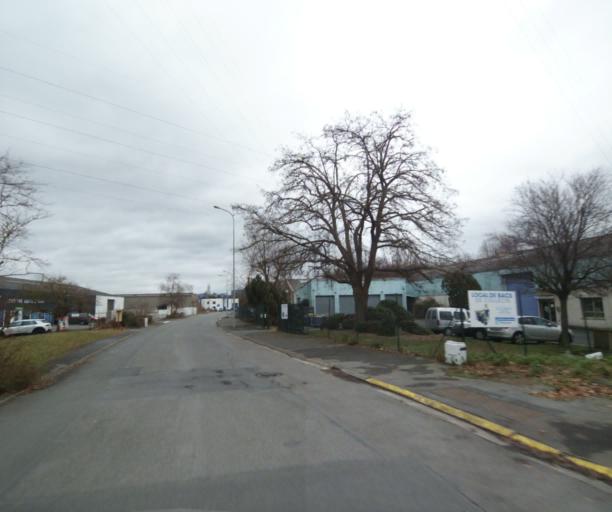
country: FR
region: Nord-Pas-de-Calais
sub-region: Departement du Nord
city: Saint-Saulve
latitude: 50.3848
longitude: 3.5559
